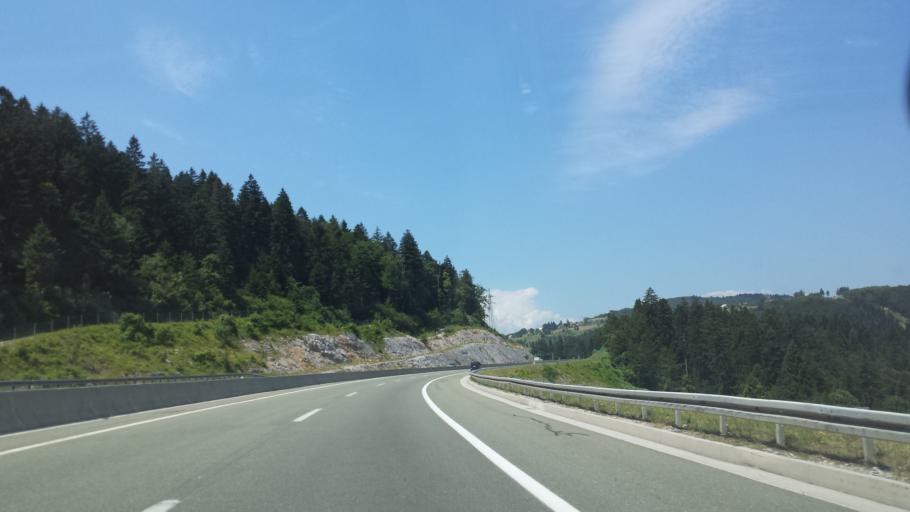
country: HR
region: Primorsko-Goranska
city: Vrbovsko
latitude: 45.3732
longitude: 14.9876
